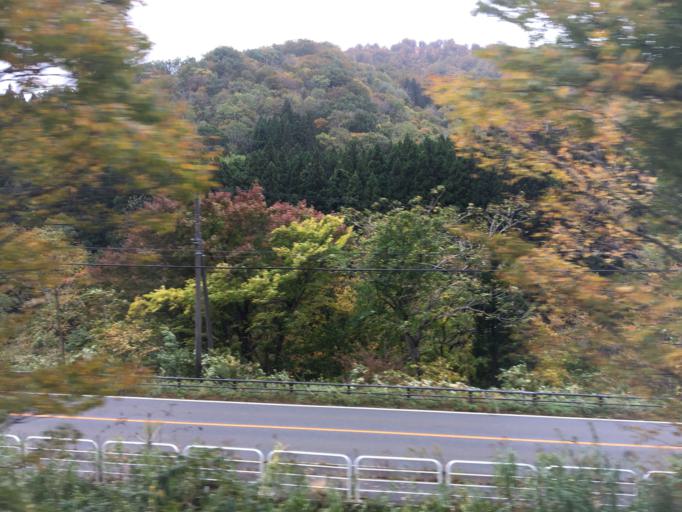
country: JP
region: Yamagata
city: Nagai
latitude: 38.0472
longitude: 139.8292
